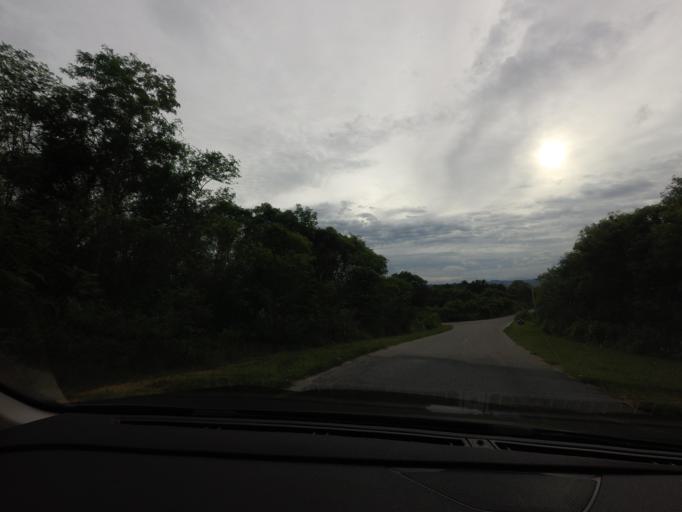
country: TH
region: Prachuap Khiri Khan
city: Hua Hin
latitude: 12.4919
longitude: 99.9434
